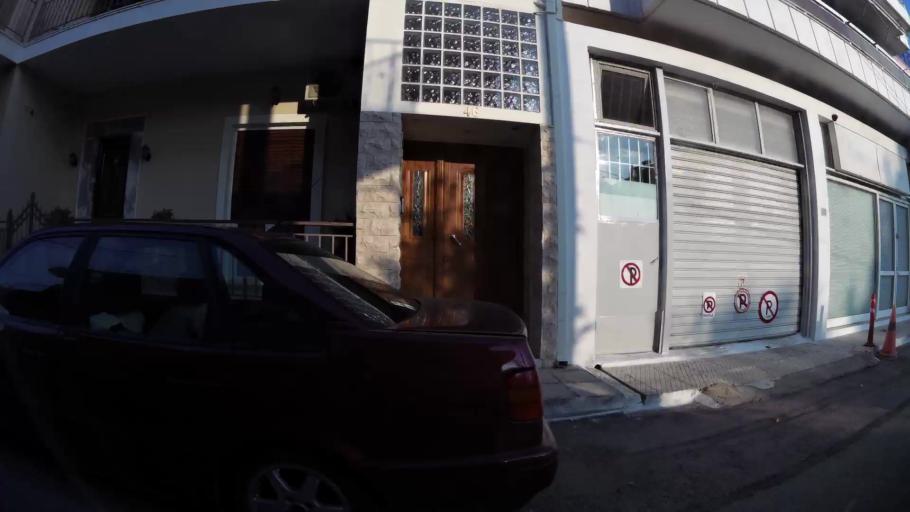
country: GR
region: Attica
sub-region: Nomarchia Anatolikis Attikis
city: Acharnes
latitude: 38.0831
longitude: 23.7345
